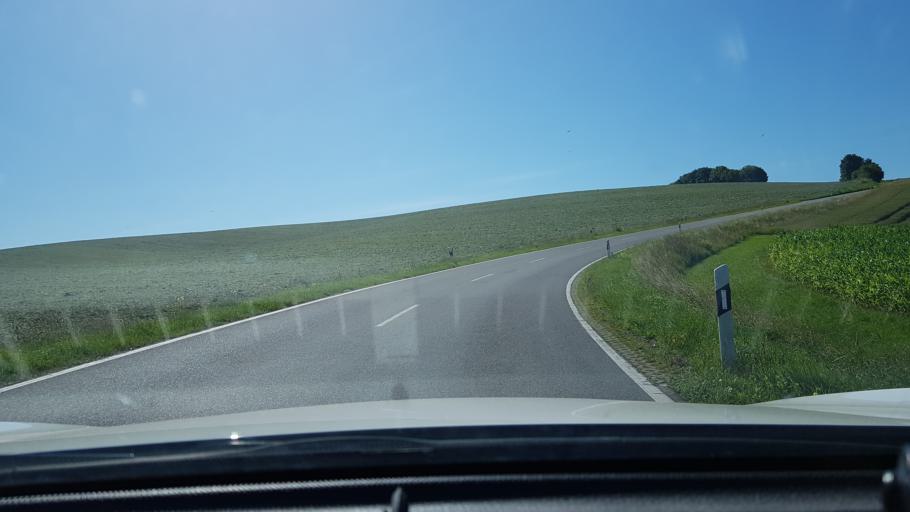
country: DE
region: Baden-Wuerttemberg
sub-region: Tuebingen Region
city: Gutenzell-Hurbel
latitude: 48.1014
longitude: 9.9620
